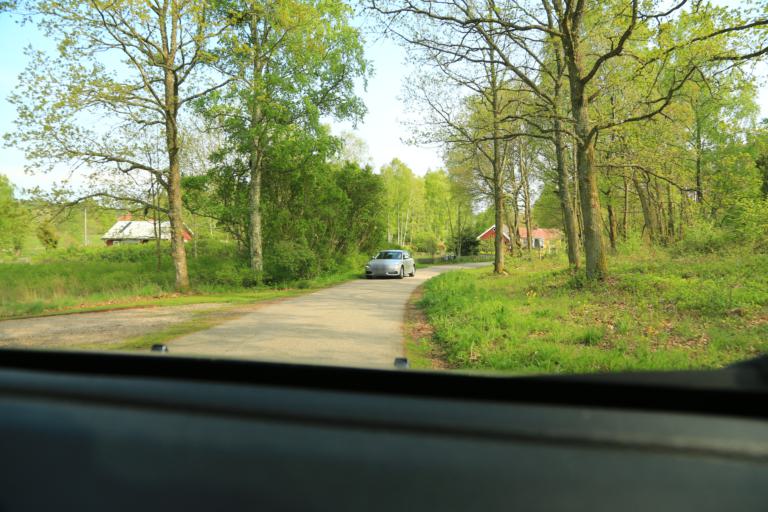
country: SE
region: Halland
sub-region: Varbergs Kommun
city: Varberg
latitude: 57.1496
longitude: 12.2267
